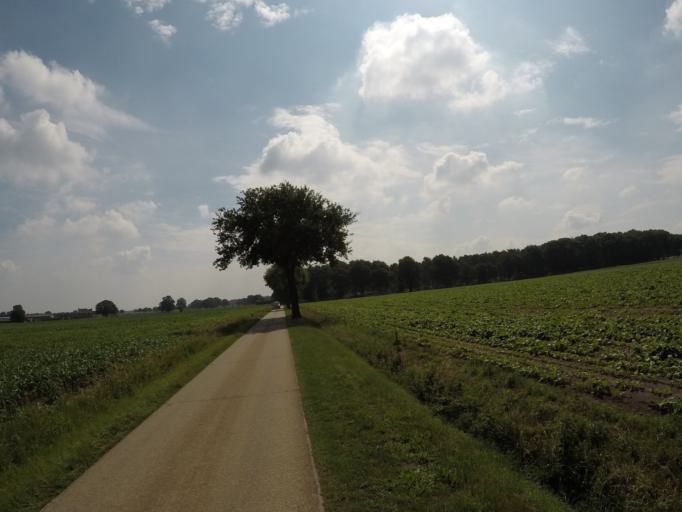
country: BE
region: Flanders
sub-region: Provincie Antwerpen
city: Brecht
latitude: 51.3338
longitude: 4.5863
